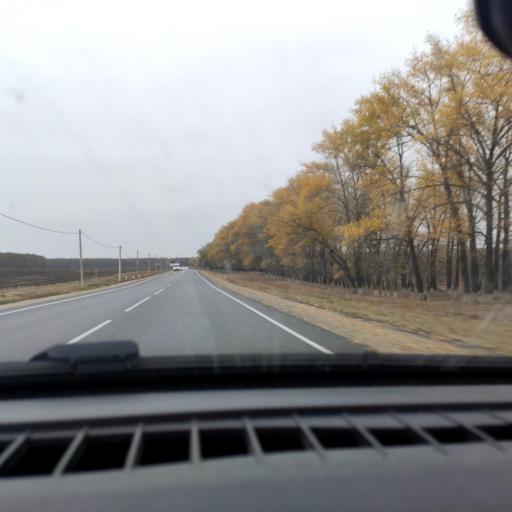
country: RU
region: Voronezj
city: Ostrogozhsk
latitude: 50.9069
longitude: 39.0663
